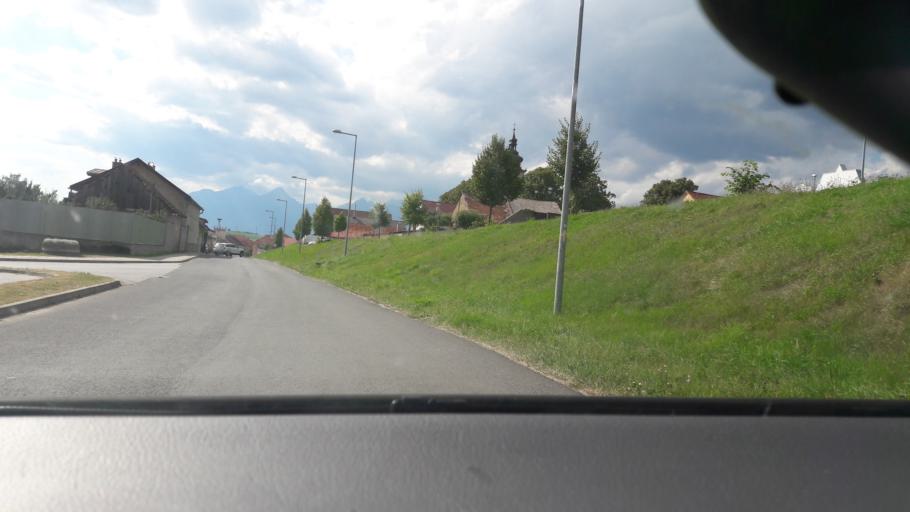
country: SK
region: Presovsky
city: Lubica
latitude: 49.1202
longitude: 20.4537
